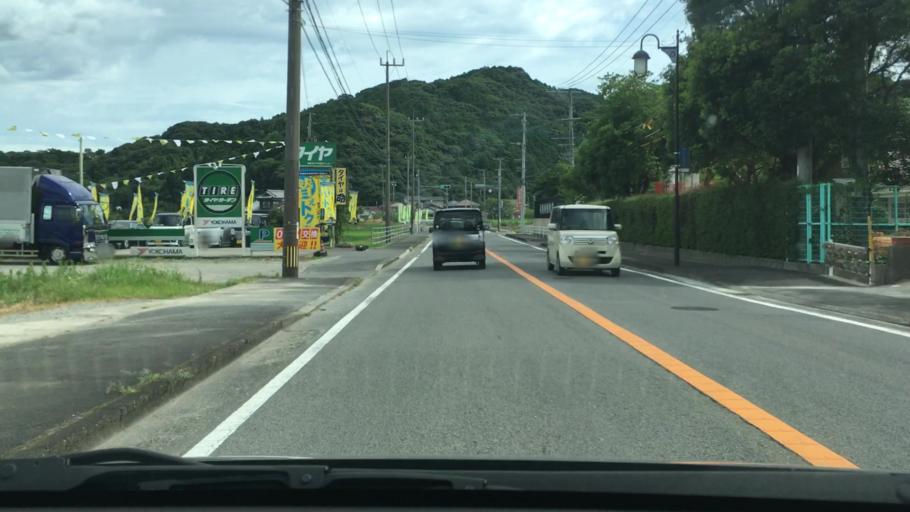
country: JP
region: Nagasaki
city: Togitsu
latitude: 32.8951
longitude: 129.7805
